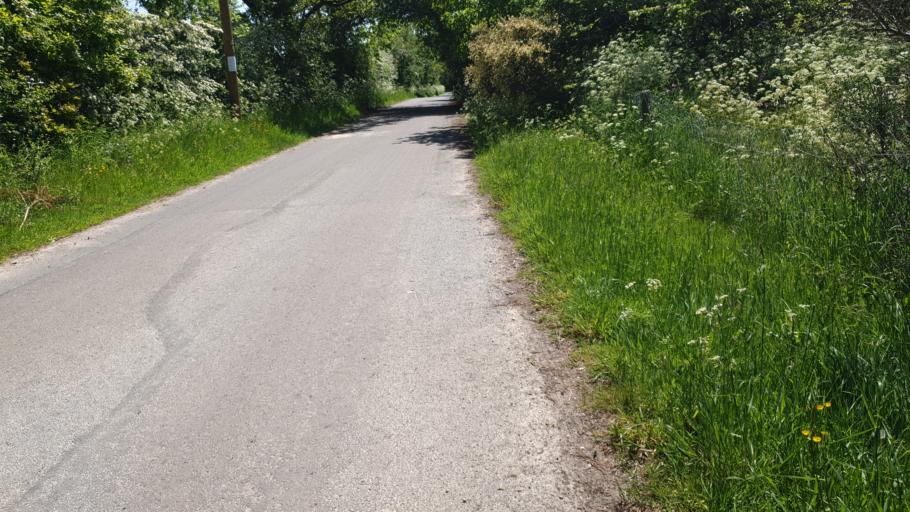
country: GB
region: England
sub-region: Essex
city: Great Bentley
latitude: 51.8920
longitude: 1.0377
